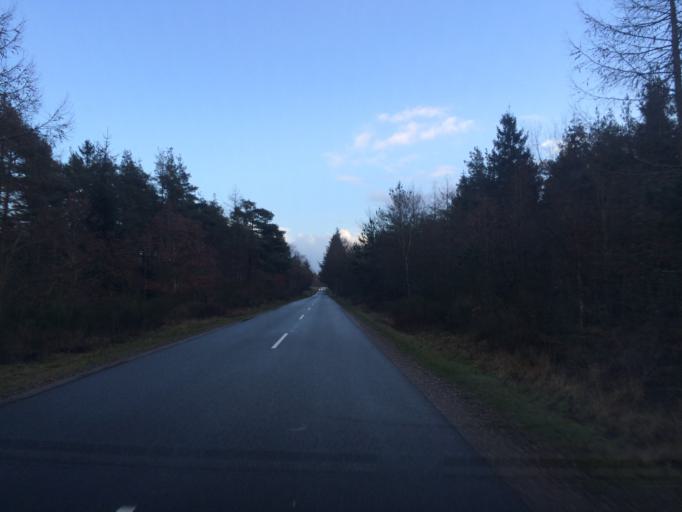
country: DK
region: Central Jutland
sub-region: Holstebro Kommune
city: Ulfborg
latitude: 56.2498
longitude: 8.3717
